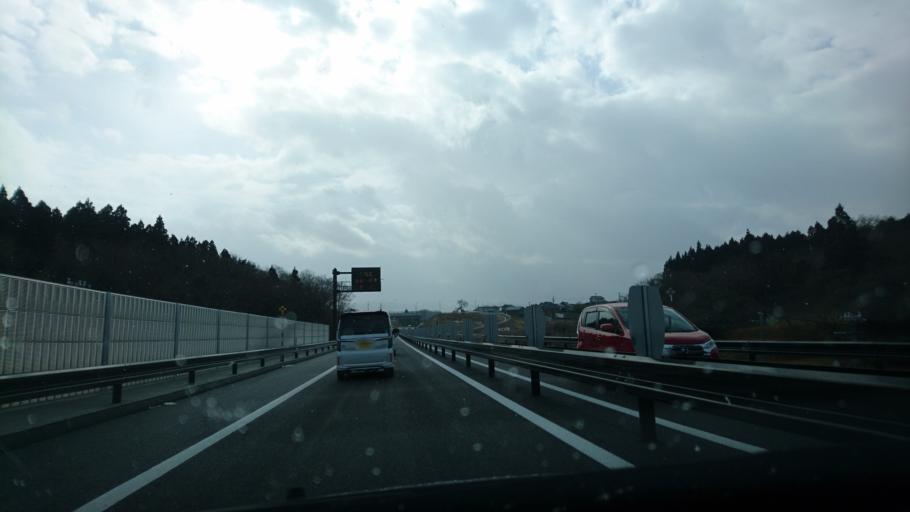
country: JP
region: Iwate
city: Ofunato
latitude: 38.7946
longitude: 141.5244
